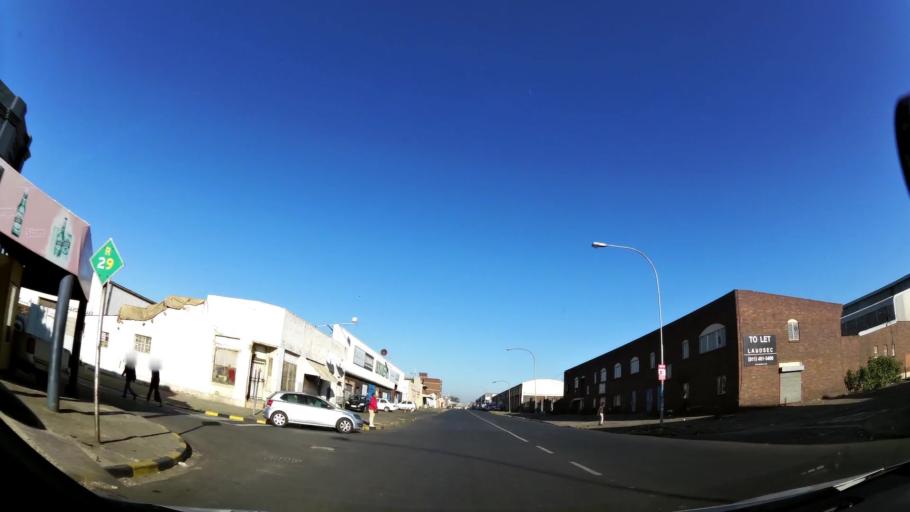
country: ZA
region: Gauteng
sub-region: City of Johannesburg Metropolitan Municipality
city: Johannesburg
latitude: -26.2052
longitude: 28.1016
